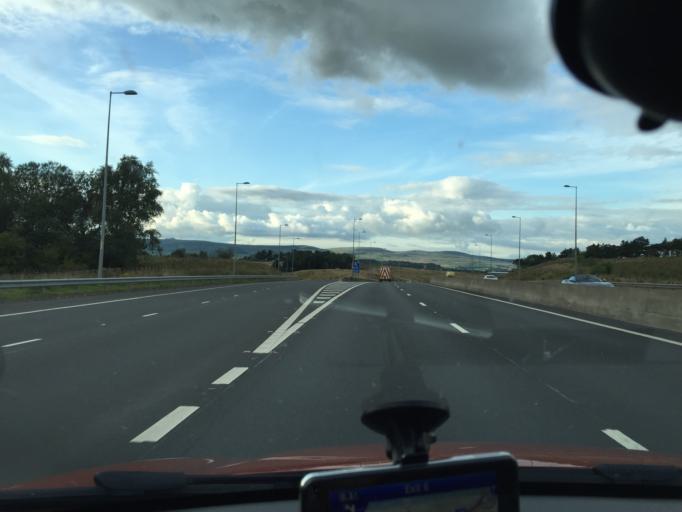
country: GB
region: Scotland
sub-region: North Lanarkshire
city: Glenboig
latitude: 55.9138
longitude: -4.0653
